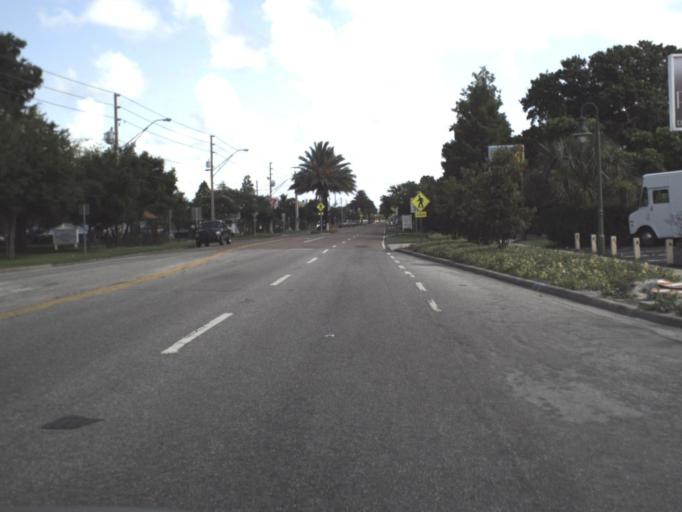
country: US
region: Florida
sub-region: Pinellas County
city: Largo
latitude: 27.9186
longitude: -82.7964
